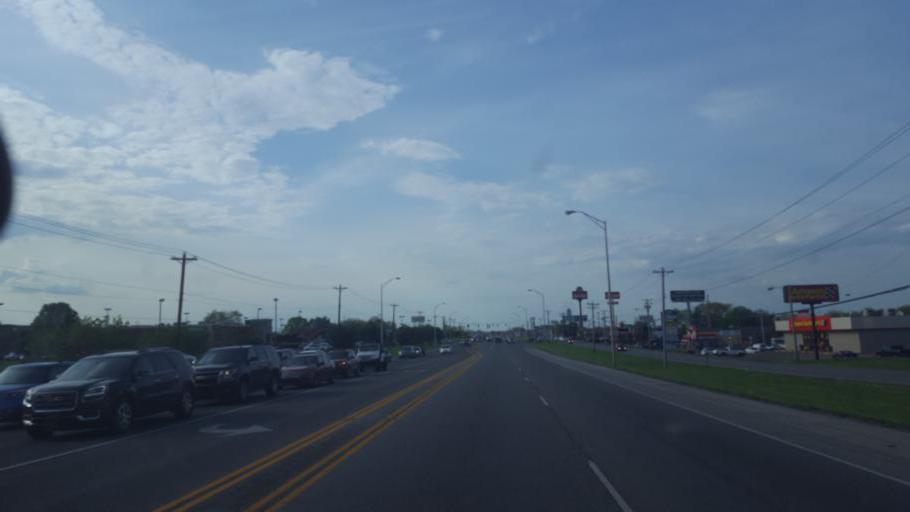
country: US
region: Kentucky
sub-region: Warren County
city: Bowling Green
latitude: 36.9465
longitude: -86.4234
